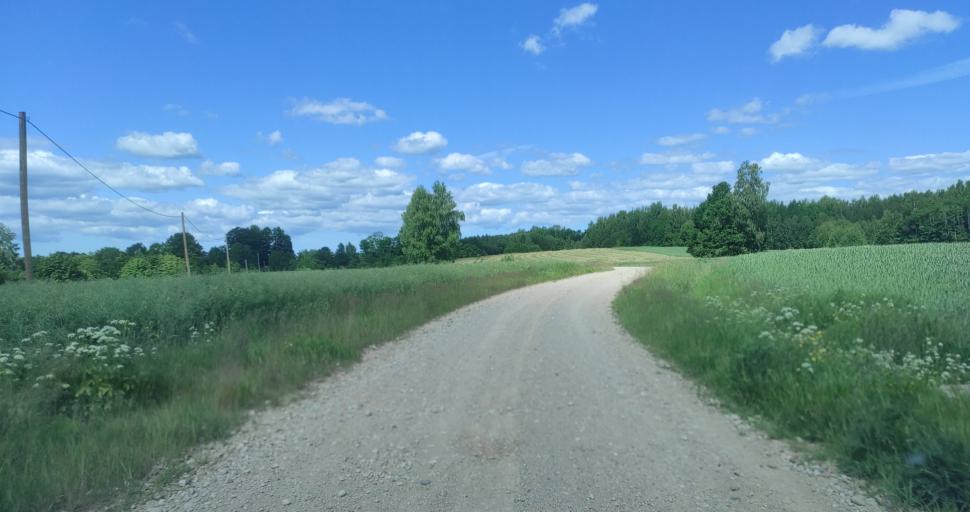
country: LV
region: Alsunga
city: Alsunga
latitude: 56.8771
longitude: 21.7131
